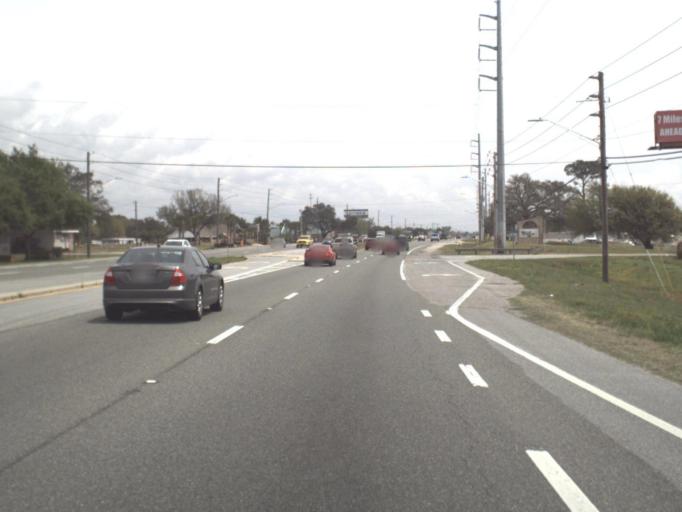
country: US
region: Florida
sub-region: Santa Rosa County
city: Oriole Beach
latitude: 30.3839
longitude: -87.1045
